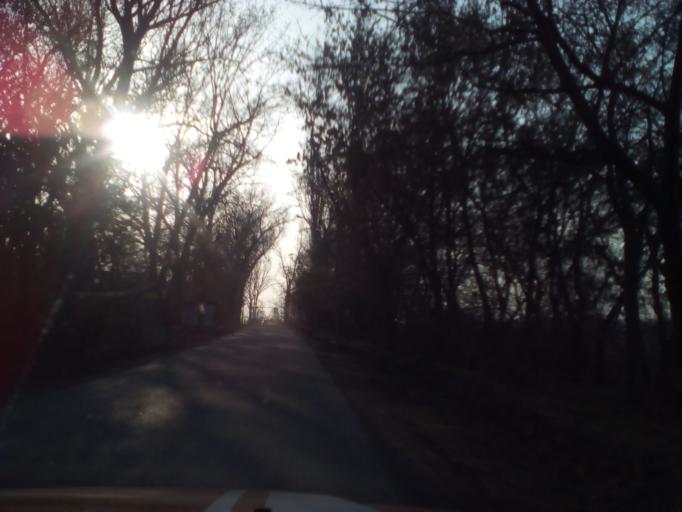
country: KZ
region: Almaty Oblysy
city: Burunday
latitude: 43.1600
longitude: 76.4529
